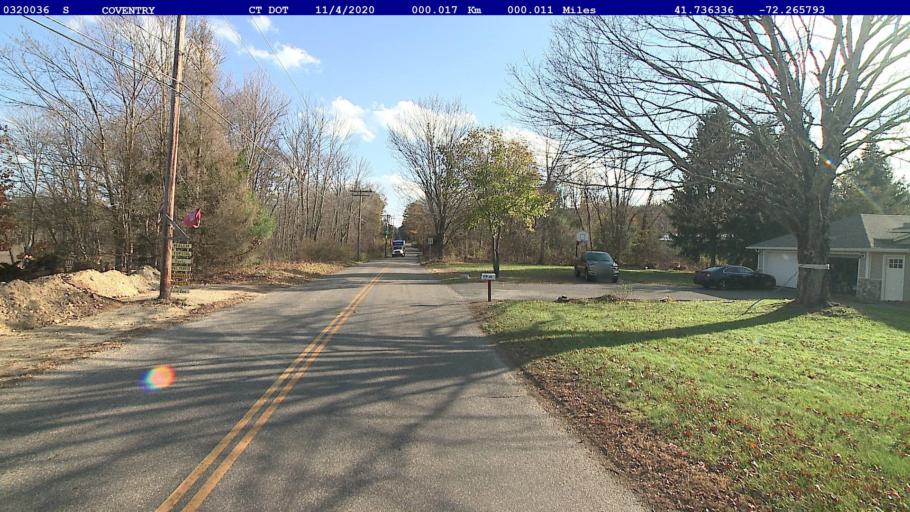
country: US
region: Connecticut
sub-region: Tolland County
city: Mansfield City
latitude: 41.7363
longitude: -72.2658
